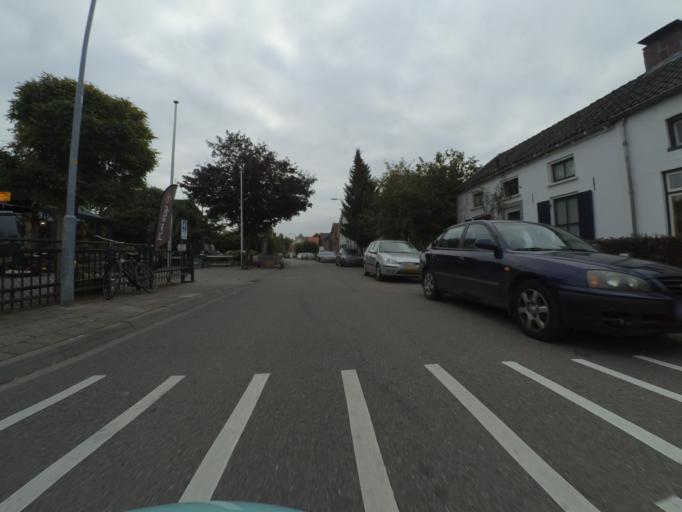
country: NL
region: Utrecht
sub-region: Gemeente Wijk bij Duurstede
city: Wijk bij Duurstede
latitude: 51.9515
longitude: 5.2884
